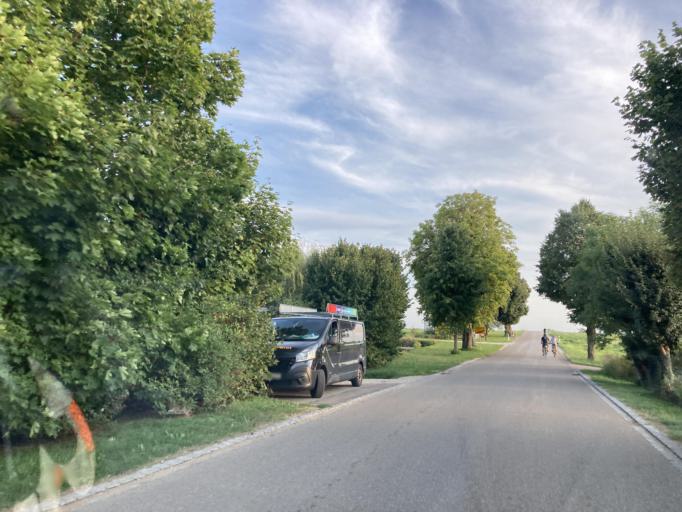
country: DE
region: Bavaria
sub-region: Swabia
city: Munningen
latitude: 48.9279
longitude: 10.6190
